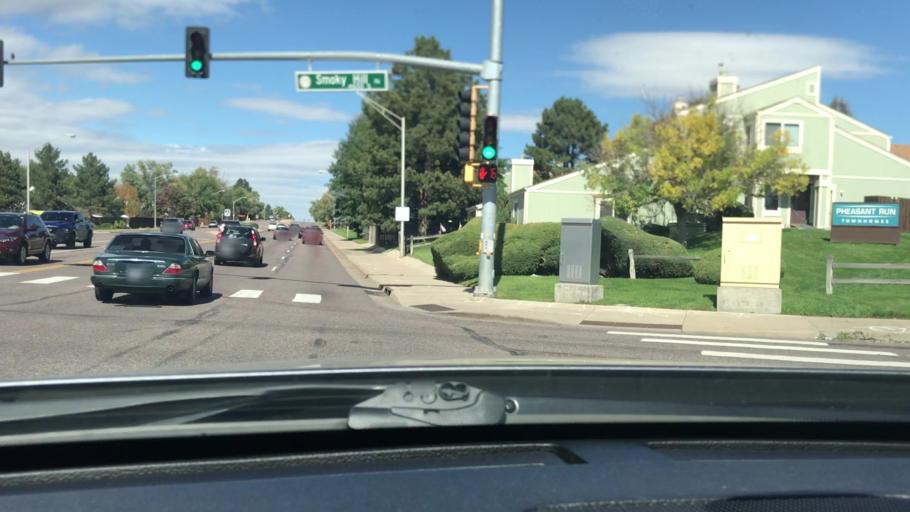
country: US
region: Colorado
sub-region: Arapahoe County
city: Dove Valley
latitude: 39.6326
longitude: -104.8102
